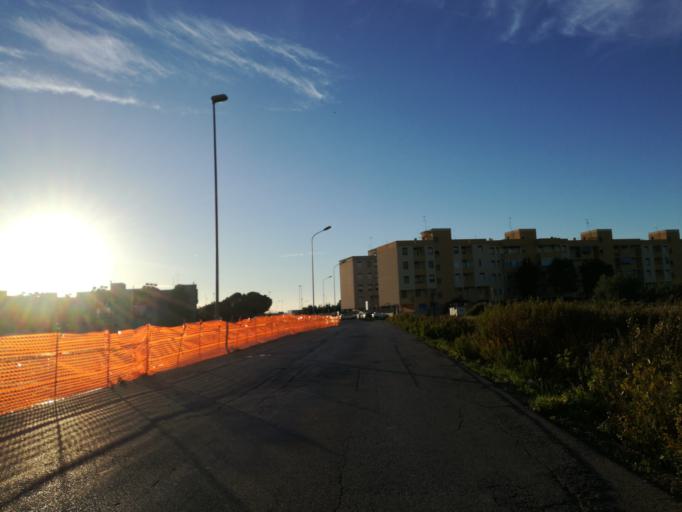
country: IT
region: Apulia
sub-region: Provincia di Bari
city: Adelfia
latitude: 41.0079
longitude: 16.8659
